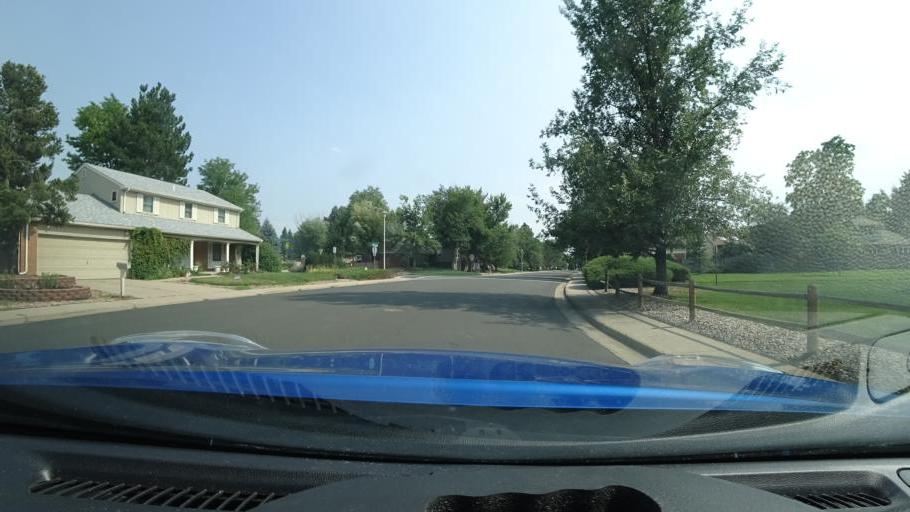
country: US
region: Colorado
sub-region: Adams County
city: Aurora
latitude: 39.6659
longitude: -104.8481
